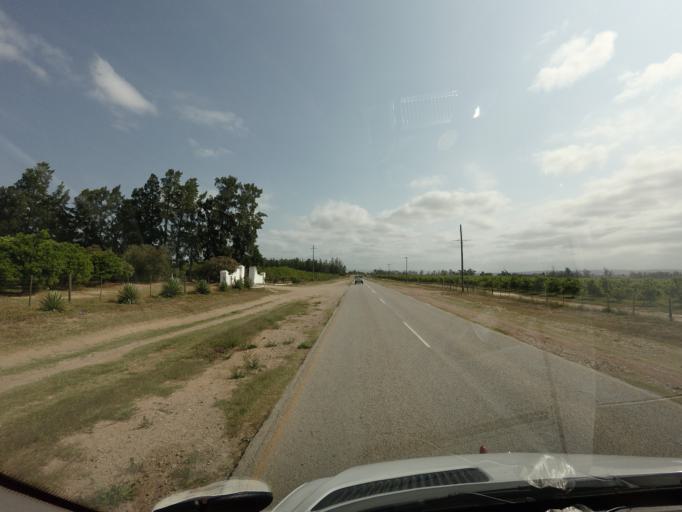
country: ZA
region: Eastern Cape
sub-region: Cacadu District Municipality
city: Kirkwood
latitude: -33.5716
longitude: 25.6794
